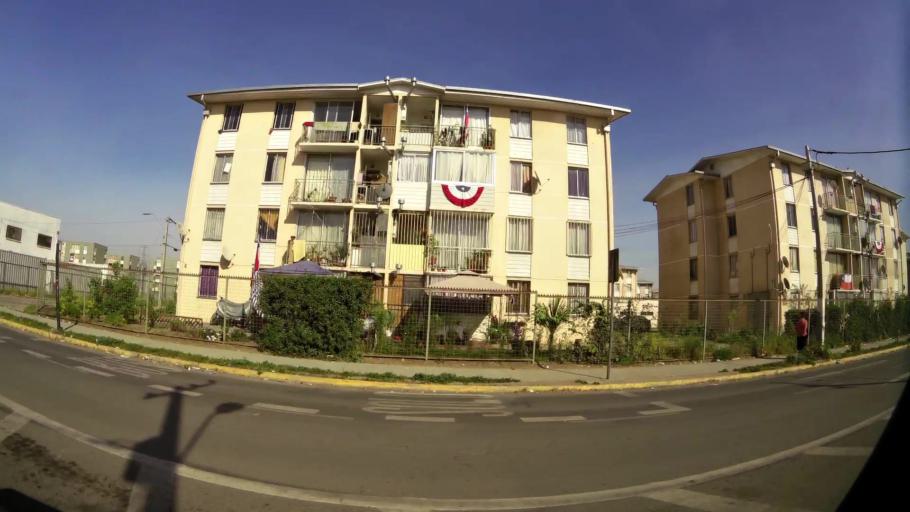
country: CL
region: Santiago Metropolitan
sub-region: Provincia de Santiago
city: Lo Prado
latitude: -33.4224
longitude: -70.7605
